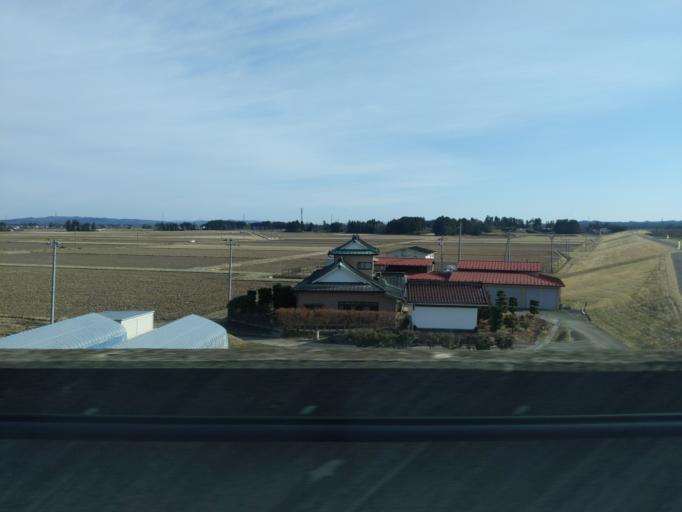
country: JP
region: Miyagi
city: Furukawa
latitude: 38.5443
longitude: 140.9615
